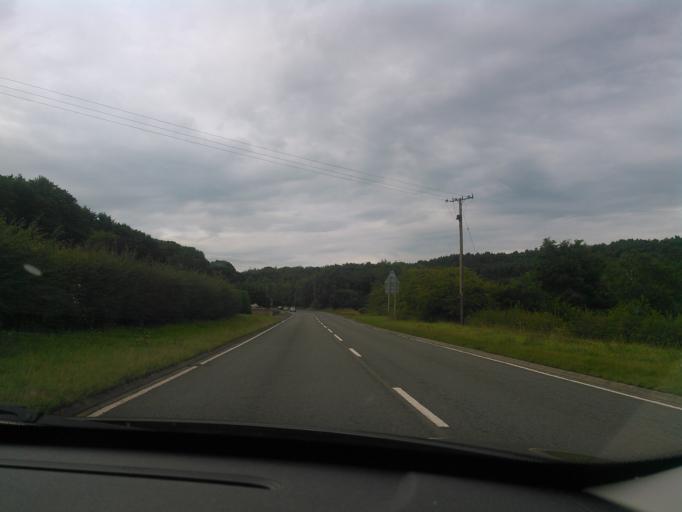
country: GB
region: England
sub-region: Shropshire
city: Prees
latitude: 52.8429
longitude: -2.6620
